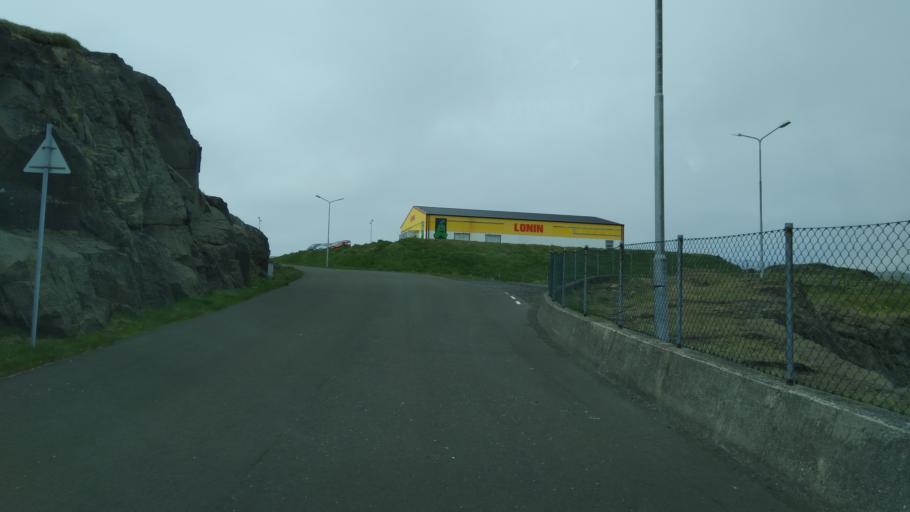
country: FO
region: Sandoy
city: Sandur
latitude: 61.9046
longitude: -6.8836
